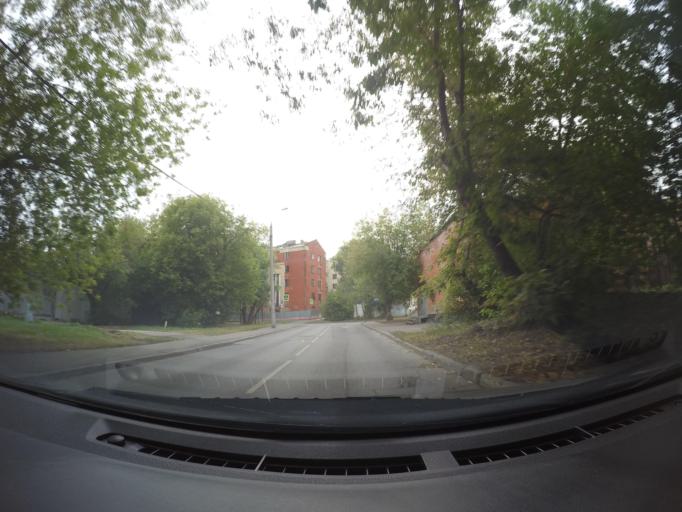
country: RU
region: Moskovskaya
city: Bogorodskoye
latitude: 55.7895
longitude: 37.7124
